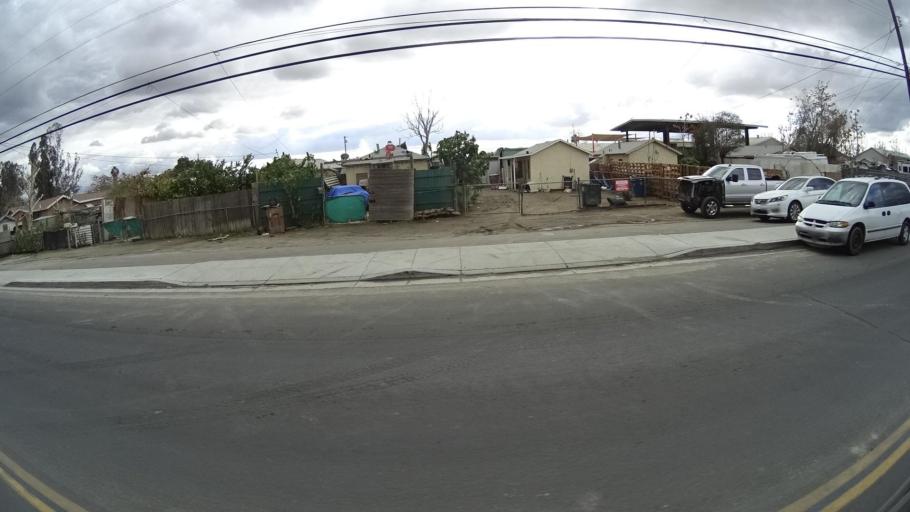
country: US
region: California
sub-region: Kern County
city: Greenfield
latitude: 35.3107
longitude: -119.0014
